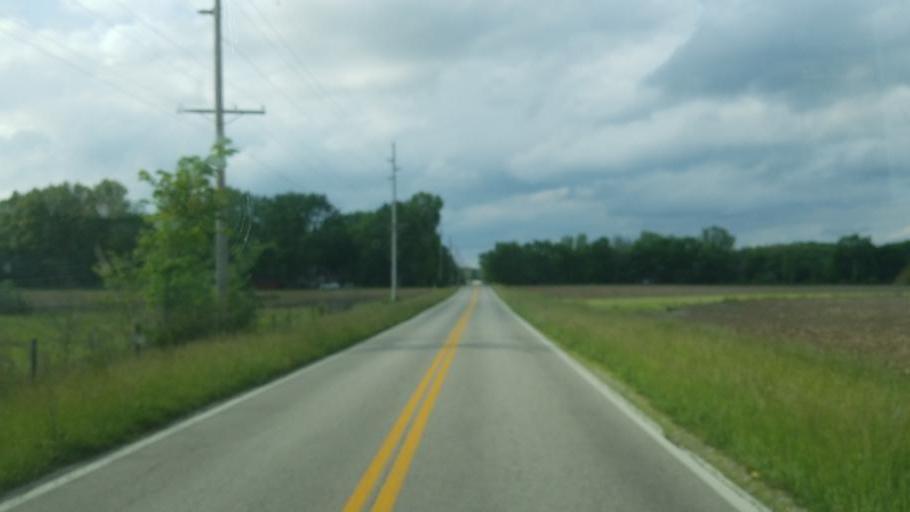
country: US
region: Ohio
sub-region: Knox County
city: Centerburg
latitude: 40.2997
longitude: -82.7848
